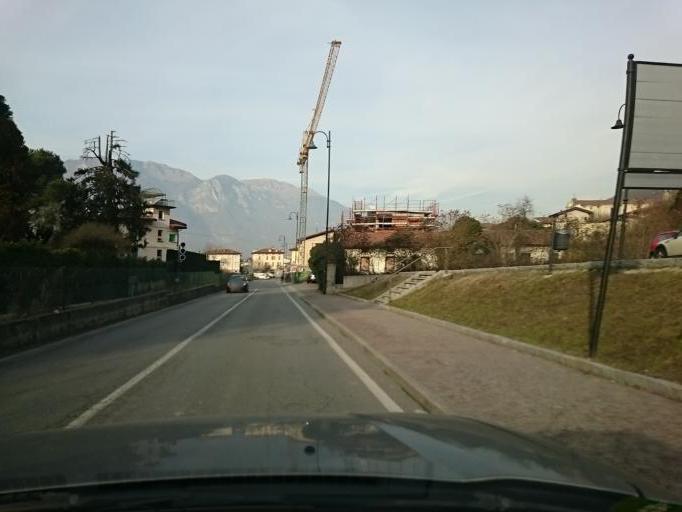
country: IT
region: Lombardy
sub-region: Provincia di Brescia
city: Pisogne
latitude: 45.8011
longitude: 10.1061
